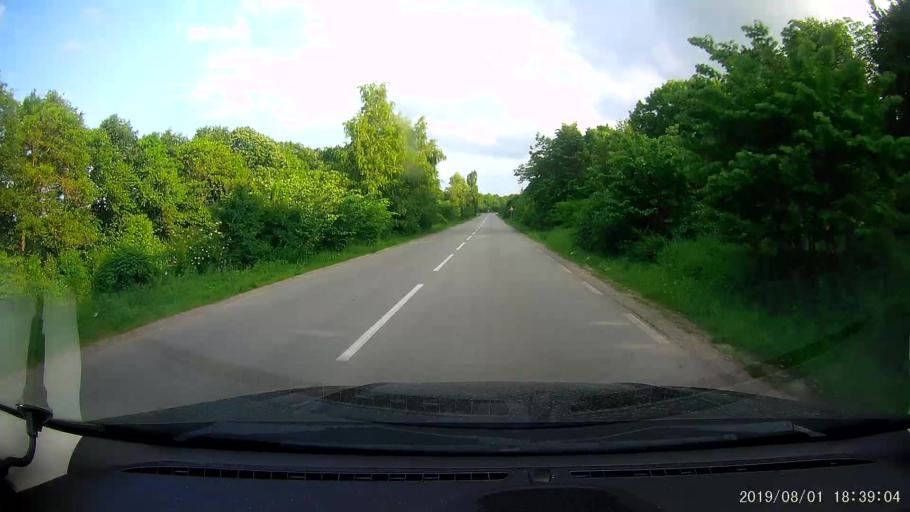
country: BG
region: Shumen
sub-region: Obshtina Khitrino
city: Gara Khitrino
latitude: 43.3932
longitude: 26.9173
